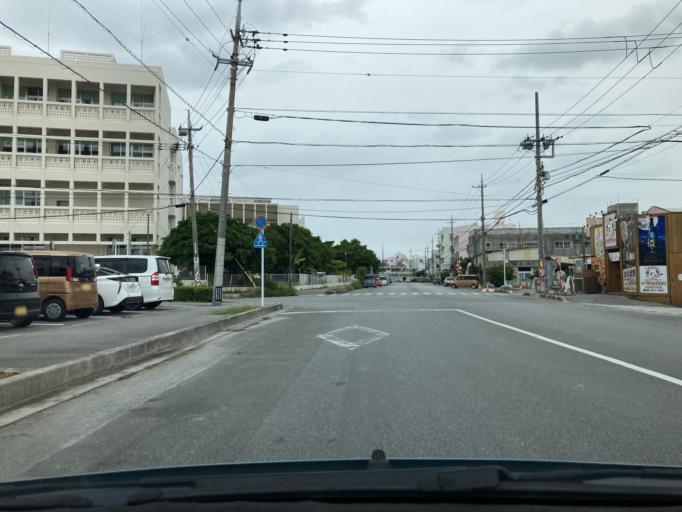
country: JP
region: Okinawa
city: Itoman
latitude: 26.1351
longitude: 127.6670
